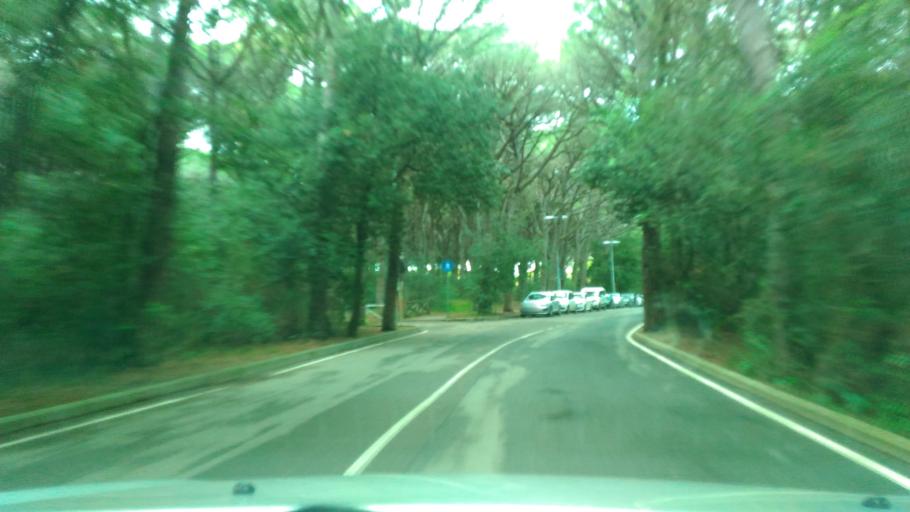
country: IT
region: Tuscany
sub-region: Provincia di Livorno
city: Cecina
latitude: 43.2929
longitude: 10.5049
